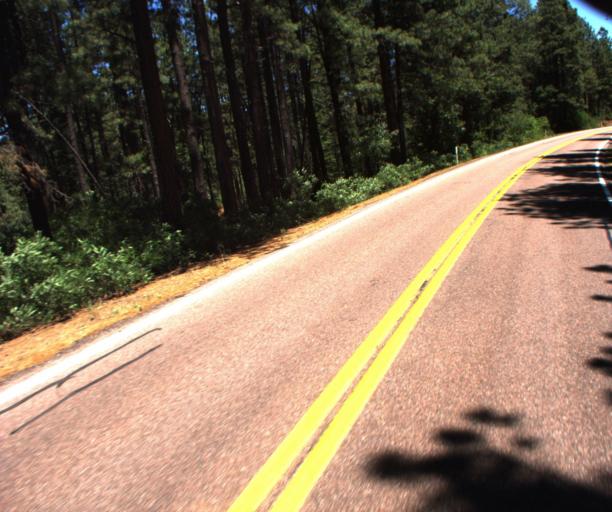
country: US
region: Arizona
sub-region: Gila County
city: Pine
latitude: 34.4617
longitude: -111.3906
